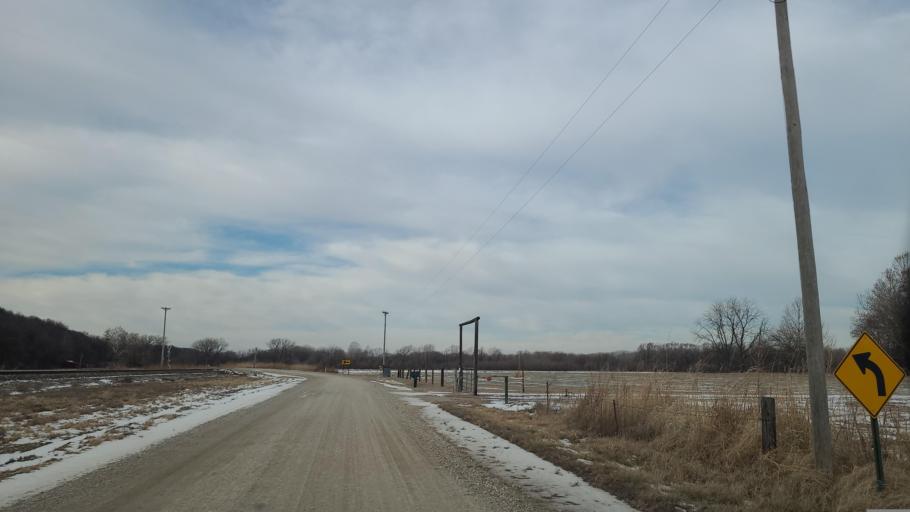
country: US
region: Kansas
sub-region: Jefferson County
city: Oskaloosa
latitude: 39.0597
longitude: -95.4599
